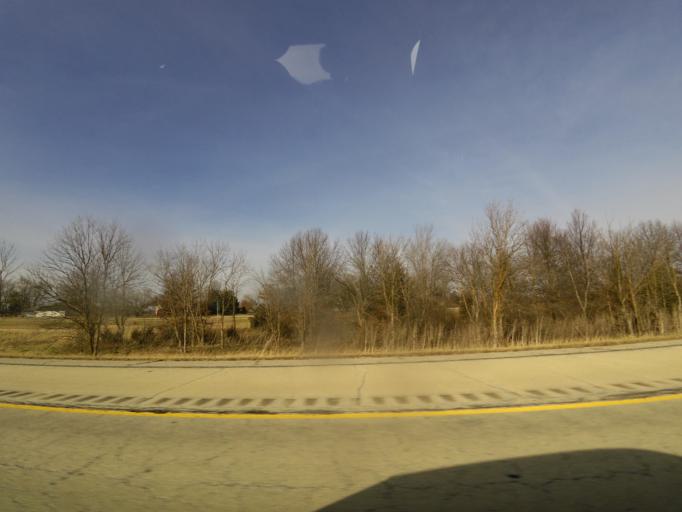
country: US
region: Illinois
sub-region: Macon County
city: Forsyth
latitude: 39.9020
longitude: -88.9956
